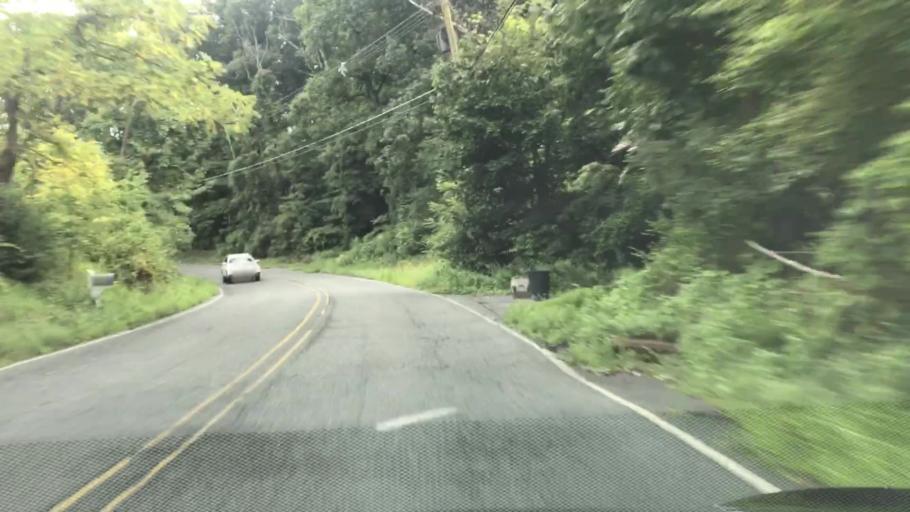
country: US
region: New Jersey
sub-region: Hunterdon County
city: Lebanon
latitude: 40.6655
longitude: -74.8572
